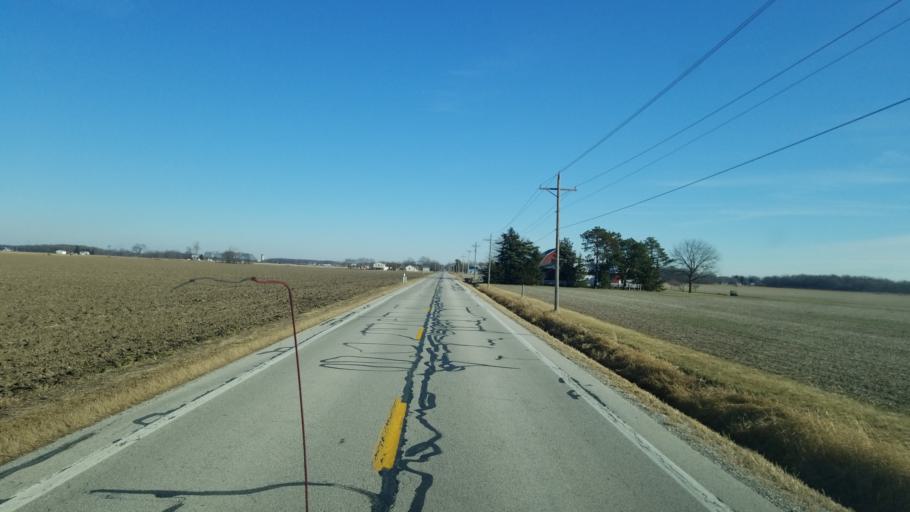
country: US
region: Ohio
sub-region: Wood County
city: Luckey
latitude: 41.4569
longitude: -83.5103
